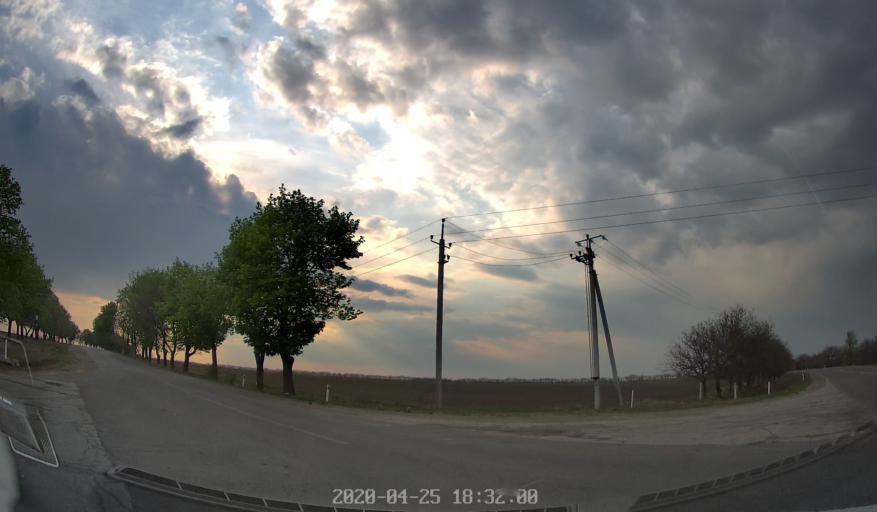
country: MD
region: Criuleni
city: Criuleni
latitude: 47.2231
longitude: 29.1453
